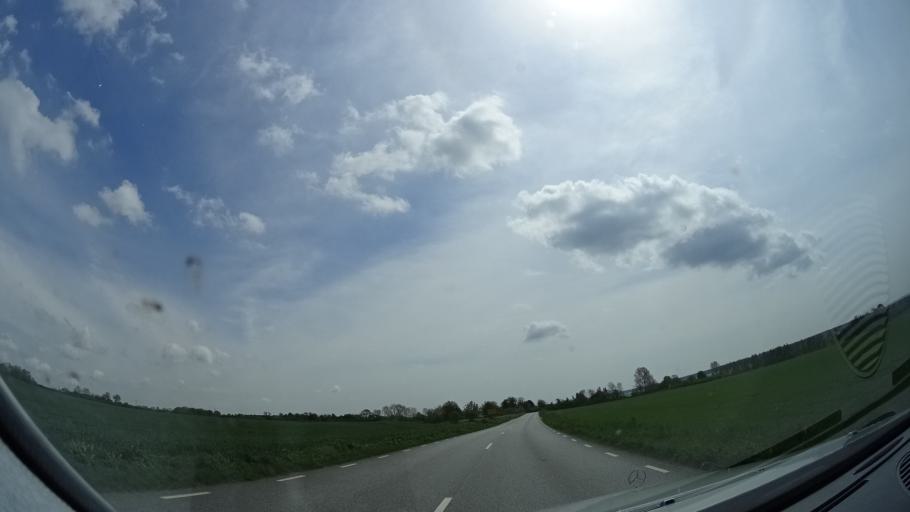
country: SE
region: Skane
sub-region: Hoors Kommun
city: Loberod
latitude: 55.7090
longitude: 13.5546
